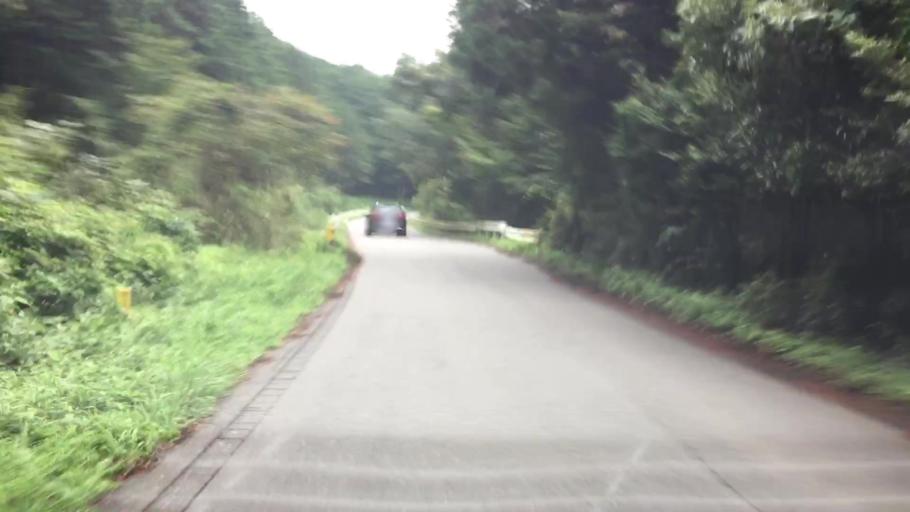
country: JP
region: Shizuoka
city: Fujinomiya
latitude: 35.3627
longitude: 138.5896
